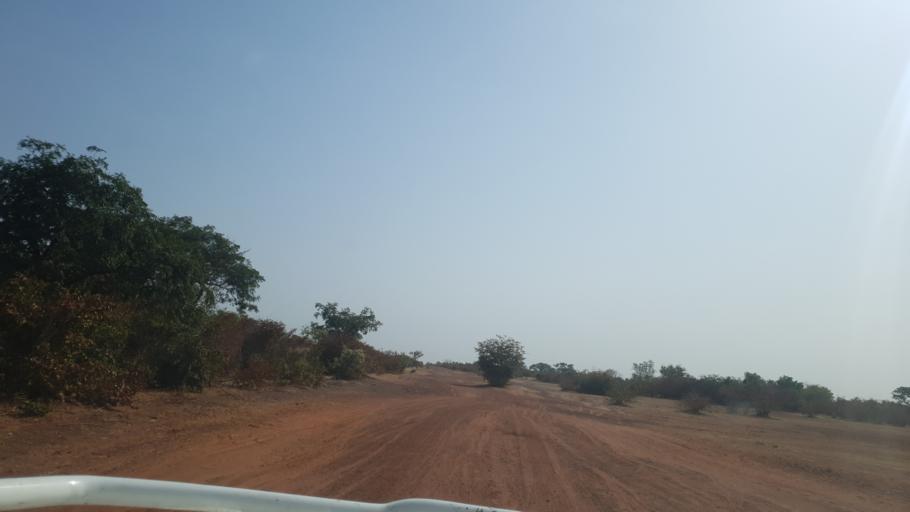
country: ML
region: Koulikoro
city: Dioila
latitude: 12.6694
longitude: -6.6678
